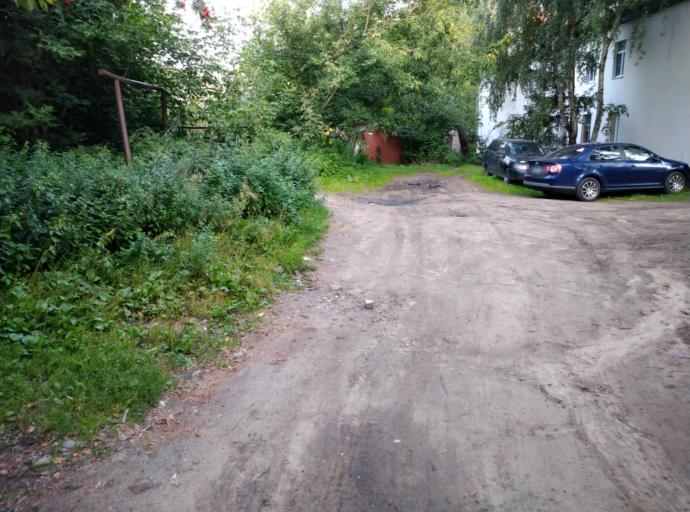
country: RU
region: Kostroma
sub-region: Kostromskoy Rayon
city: Kostroma
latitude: 57.7639
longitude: 40.9314
